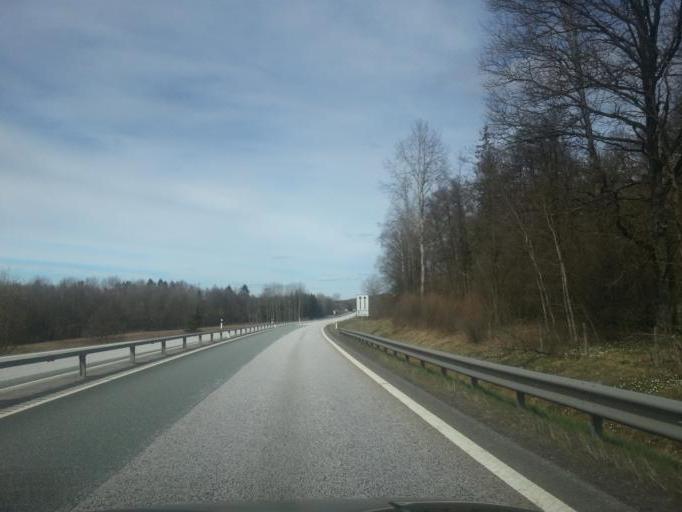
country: SE
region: Joenkoeping
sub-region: Jonkopings Kommun
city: Bankeryd
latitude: 57.8076
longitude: 14.0971
